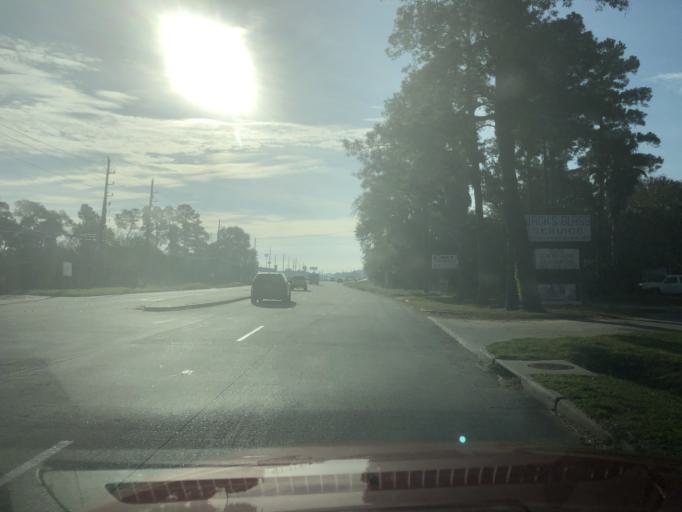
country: US
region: Texas
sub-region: Harris County
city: Spring
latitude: 30.0111
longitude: -95.4669
